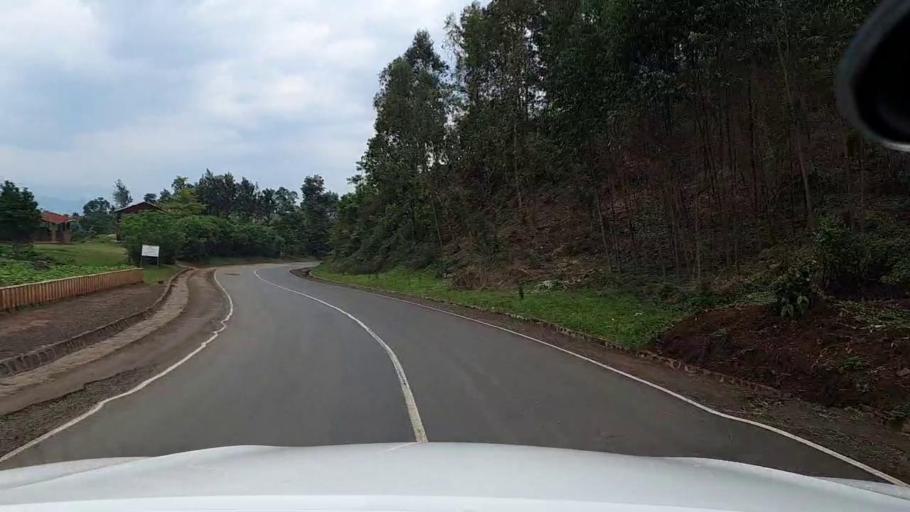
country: RW
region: Western Province
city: Cyangugu
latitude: -2.6573
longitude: 28.9716
